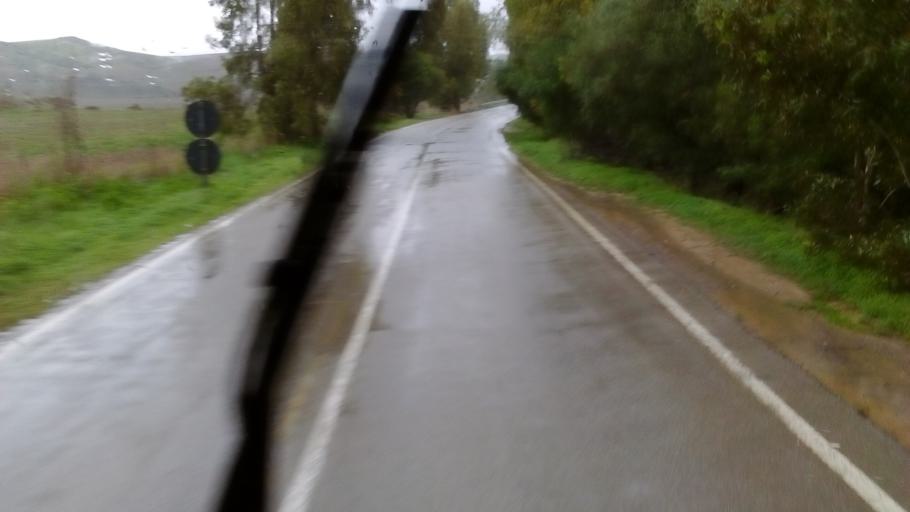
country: IT
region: Sicily
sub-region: Enna
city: Pietraperzia
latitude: 37.4921
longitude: 14.1514
